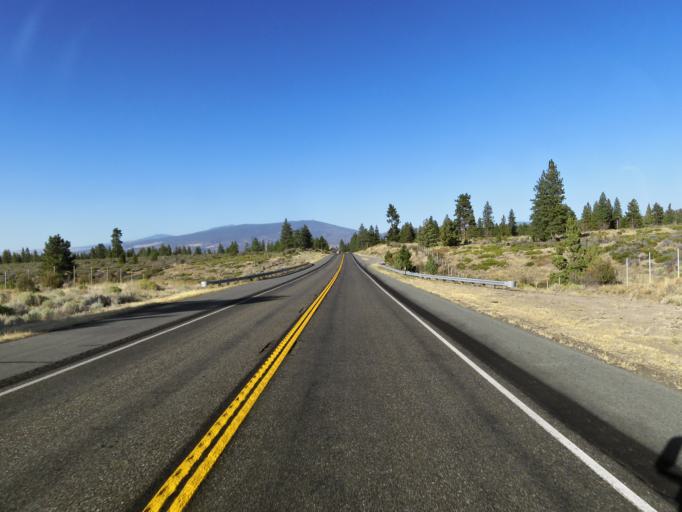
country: US
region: California
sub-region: Siskiyou County
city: Weed
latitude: 41.4949
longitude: -122.3316
